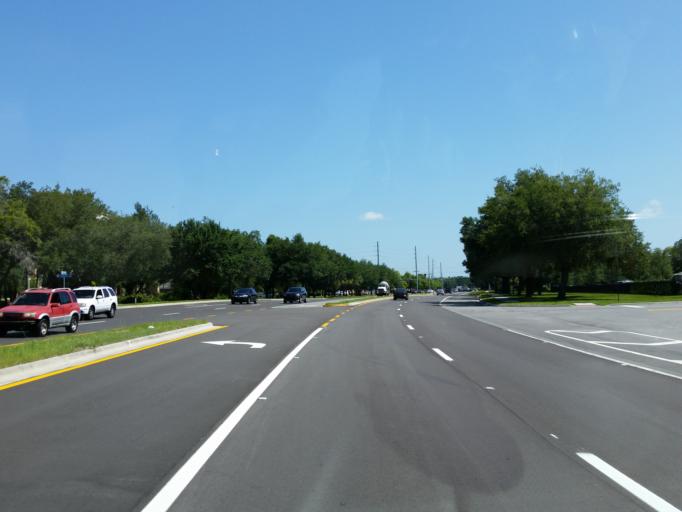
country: US
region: Florida
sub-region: Hillsborough County
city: Palm River-Clair Mel
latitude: 27.9383
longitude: -82.3379
